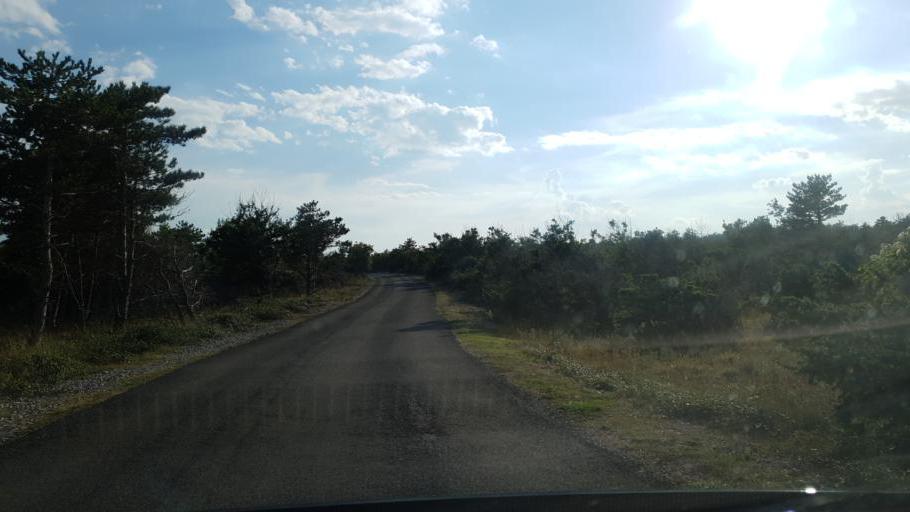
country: HR
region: Primorsko-Goranska
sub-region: Grad Crikvenica
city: Jadranovo
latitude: 45.1808
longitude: 14.6112
